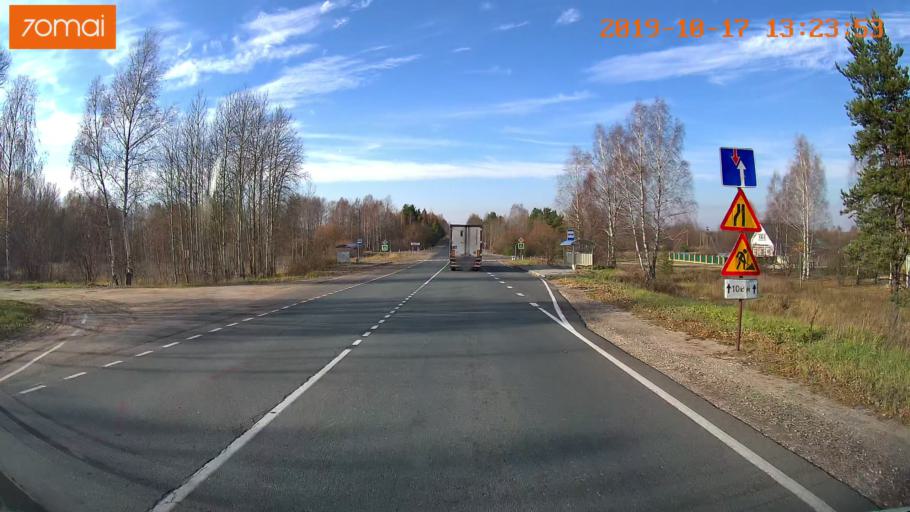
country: RU
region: Rjazan
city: Gus'-Zheleznyy
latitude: 55.0920
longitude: 40.9724
